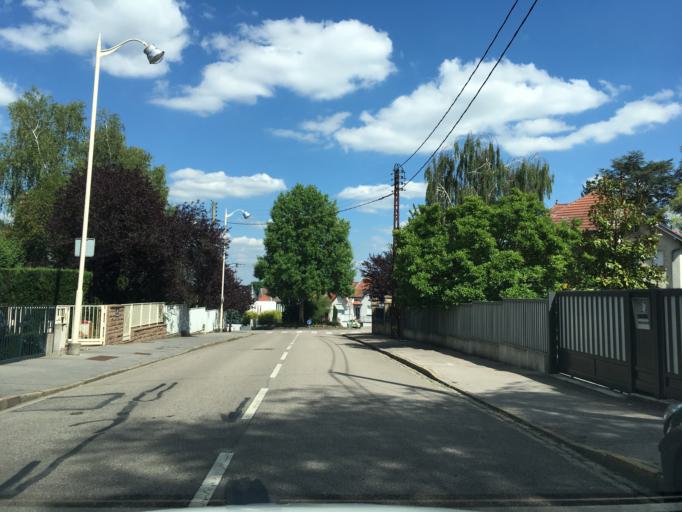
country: FR
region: Lorraine
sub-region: Departement de Meurthe-et-Moselle
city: Laxou
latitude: 48.6944
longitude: 6.1454
